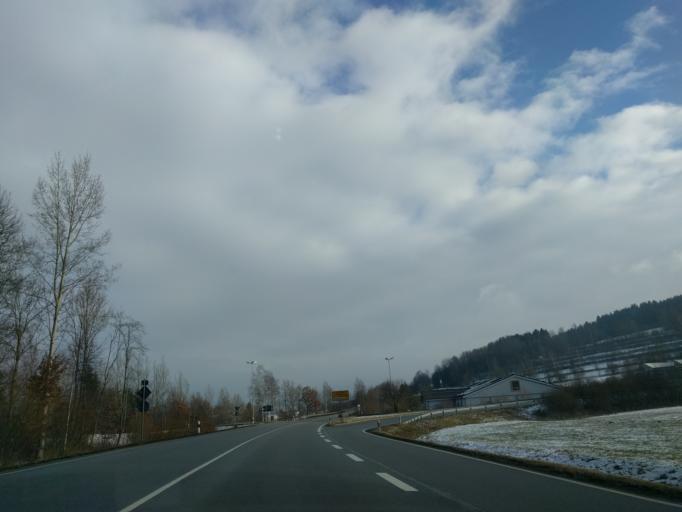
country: DE
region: Bavaria
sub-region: Lower Bavaria
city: Zwiesel
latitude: 49.0005
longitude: 13.2167
